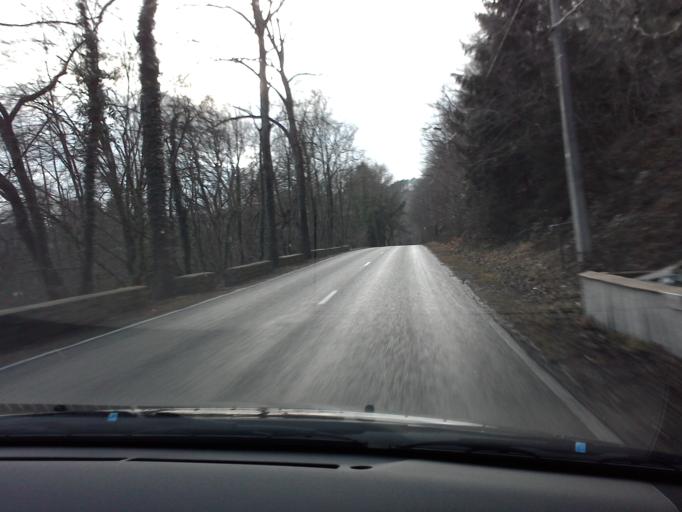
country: BE
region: Wallonia
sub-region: Province de Liege
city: Aywaille
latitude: 50.4703
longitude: 5.7353
